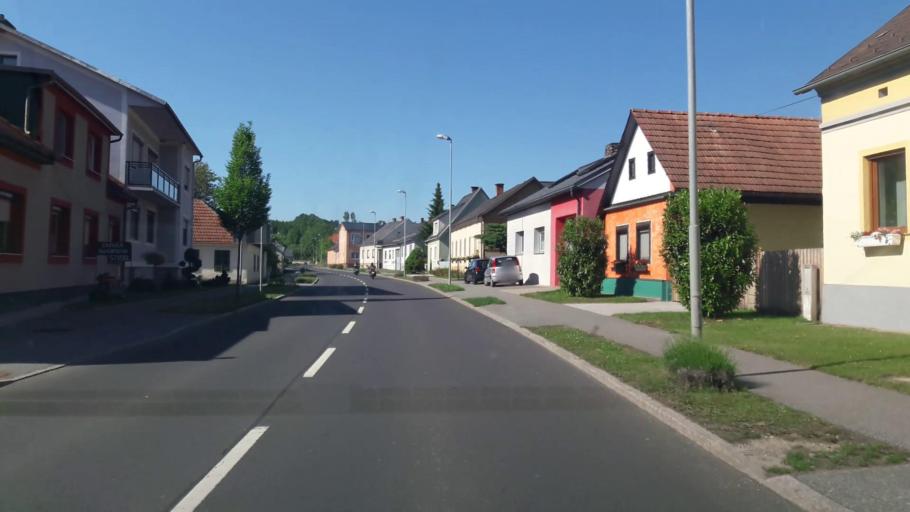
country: AT
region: Burgenland
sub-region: Politischer Bezirk Gussing
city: Ollersdorf im Burgenland
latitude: 47.1847
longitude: 16.1642
